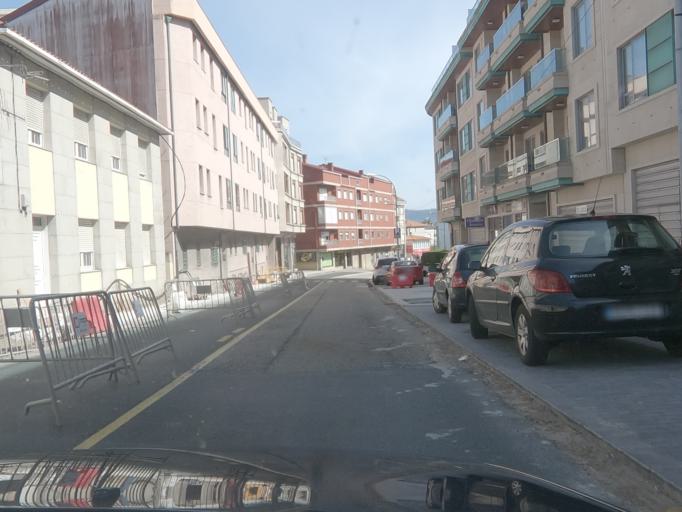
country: ES
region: Galicia
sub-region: Provincia de Pontevedra
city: Sanxenxo
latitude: 42.4042
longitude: -8.8103
